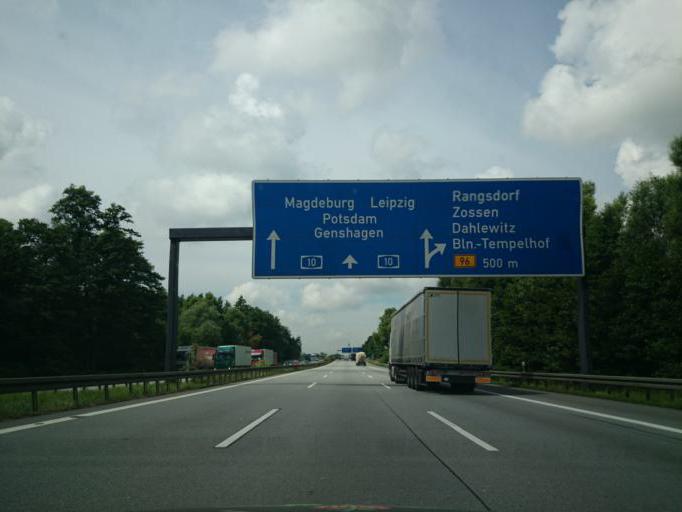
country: DE
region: Brandenburg
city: Rangsdorf
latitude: 52.3105
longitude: 13.4636
